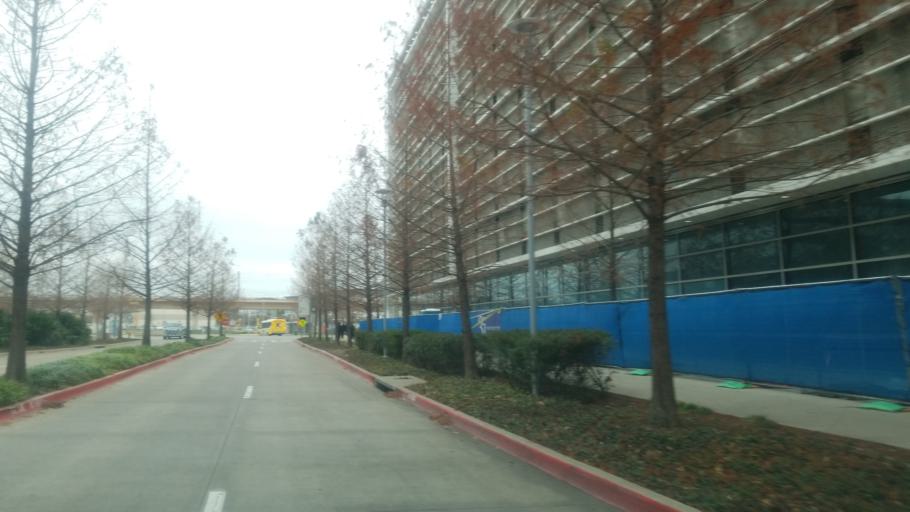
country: US
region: Texas
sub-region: Dallas County
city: Dallas
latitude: 32.8122
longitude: -96.8350
